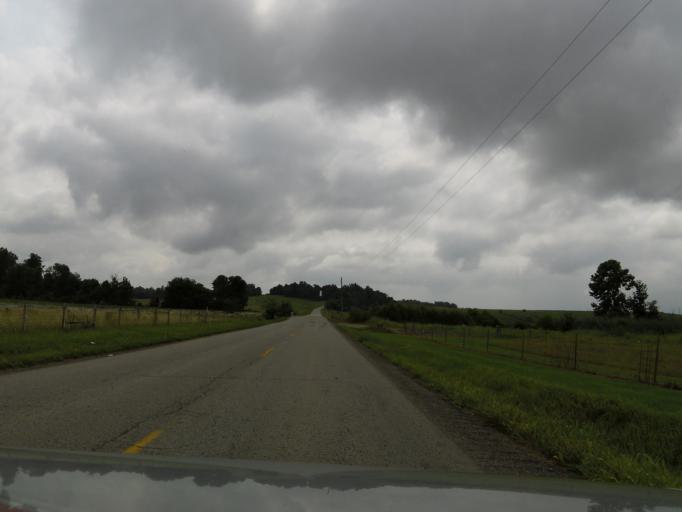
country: US
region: Kentucky
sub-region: Hopkins County
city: Madisonville
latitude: 37.3293
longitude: -87.3999
